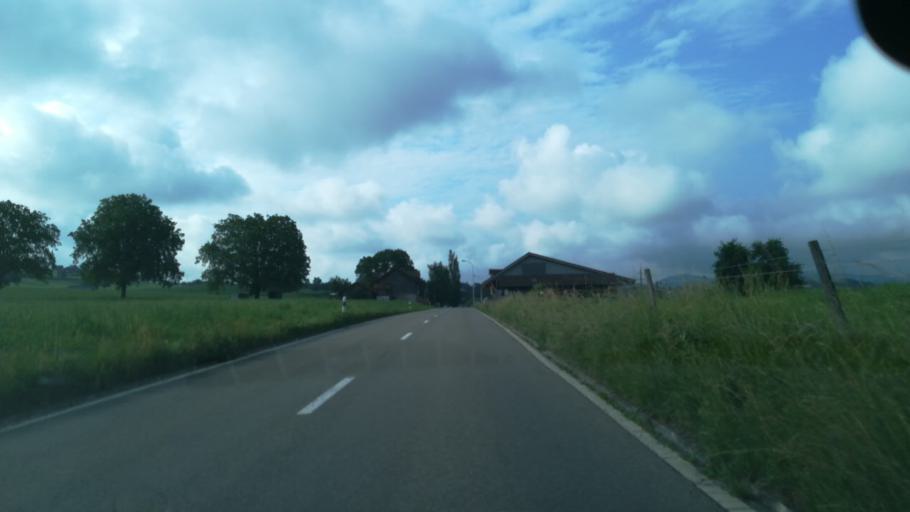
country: CH
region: Saint Gallen
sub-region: Wahlkreis St. Gallen
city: Andwil
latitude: 47.4531
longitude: 9.2535
